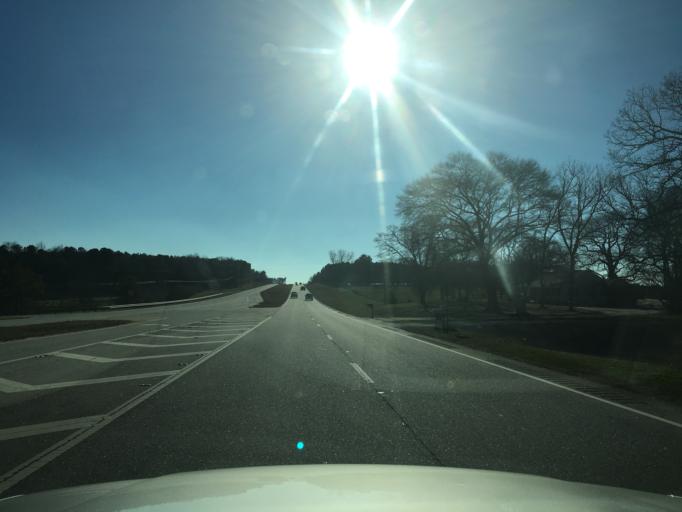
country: US
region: Georgia
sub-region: Carroll County
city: Carrollton
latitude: 33.4979
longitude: -85.0842
